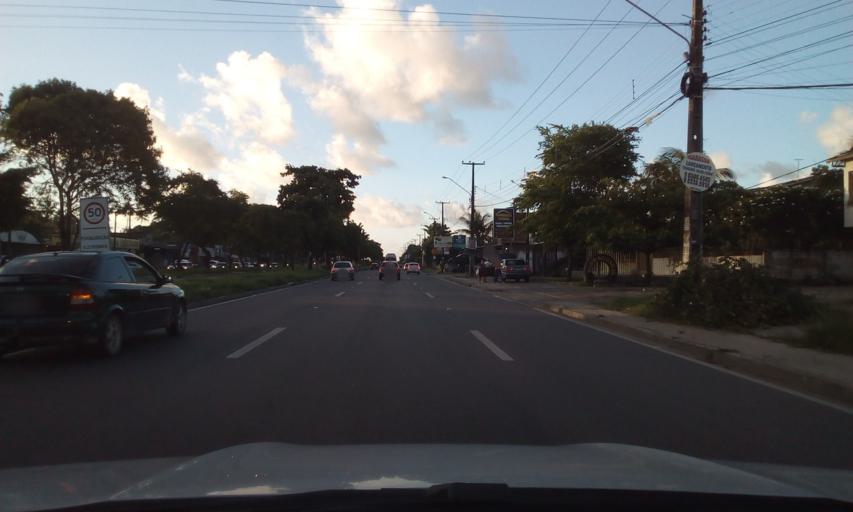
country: BR
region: Pernambuco
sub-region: Igarassu
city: Igarassu
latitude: -7.8635
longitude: -34.9074
